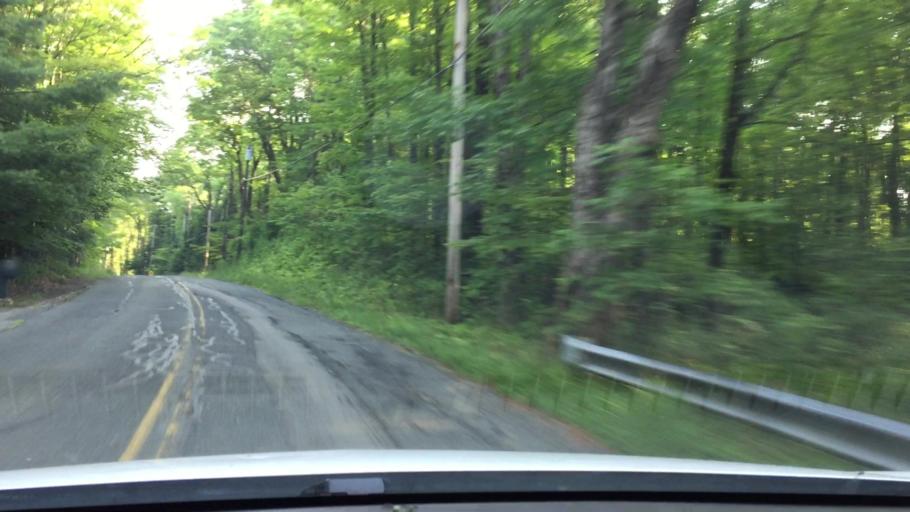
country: US
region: Massachusetts
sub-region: Berkshire County
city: Otis
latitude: 42.2445
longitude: -73.1117
